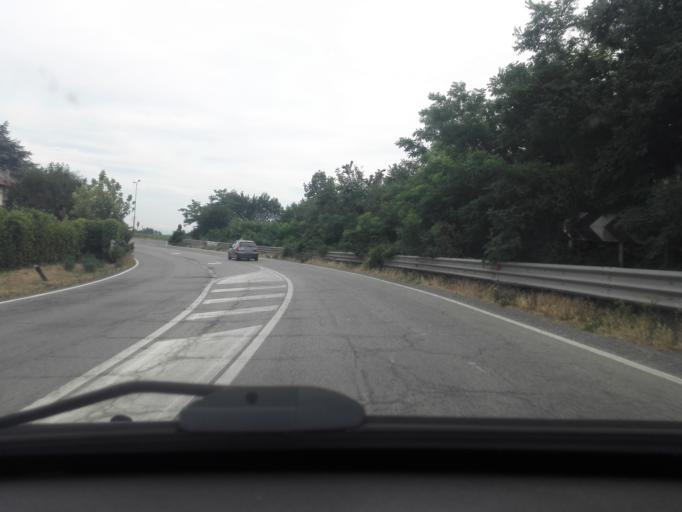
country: IT
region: Piedmont
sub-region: Provincia di Alessandria
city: Pozzolo Formigaro
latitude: 44.7923
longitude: 8.7765
